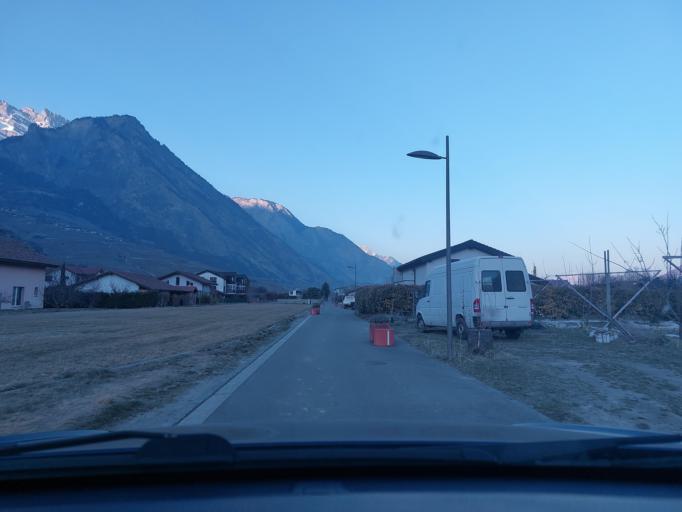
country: CH
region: Valais
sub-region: Martigny District
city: Saillon
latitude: 46.1703
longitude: 7.1897
